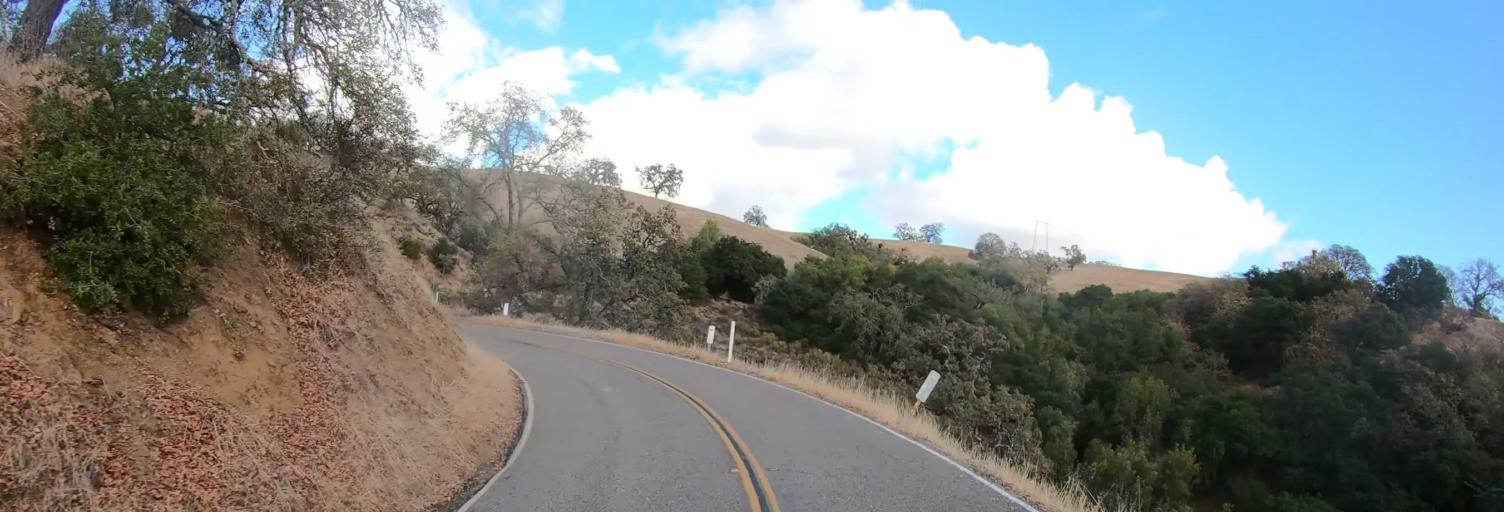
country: US
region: California
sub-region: Santa Clara County
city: East Foothills
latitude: 37.3311
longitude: -121.6883
